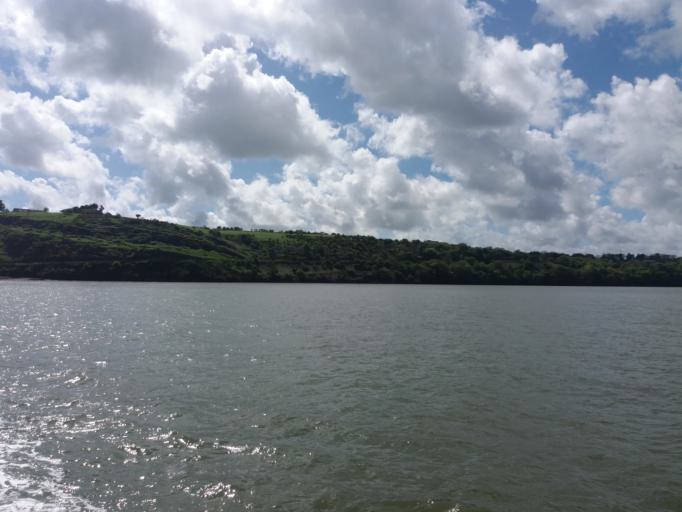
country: IE
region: Munster
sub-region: Waterford
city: Dunmore East
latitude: 52.2436
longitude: -6.9709
